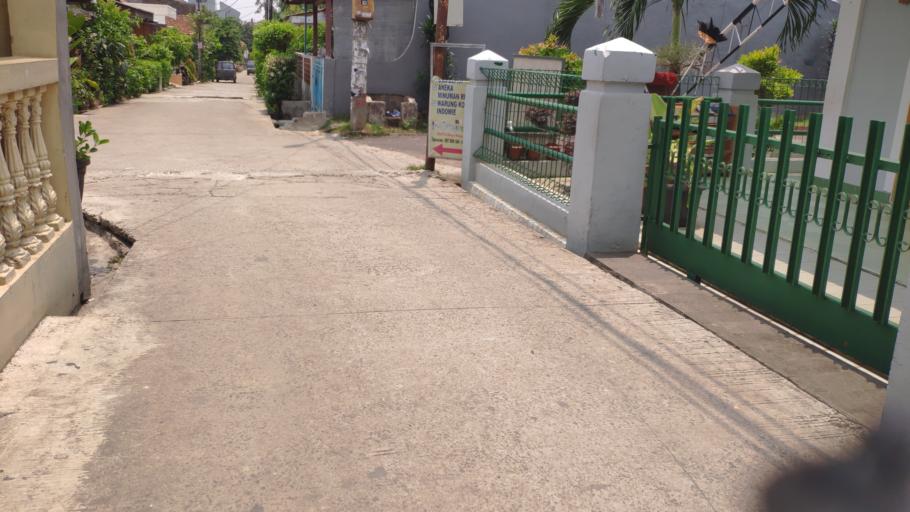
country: ID
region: West Java
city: Pamulang
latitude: -6.3375
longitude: 106.7961
